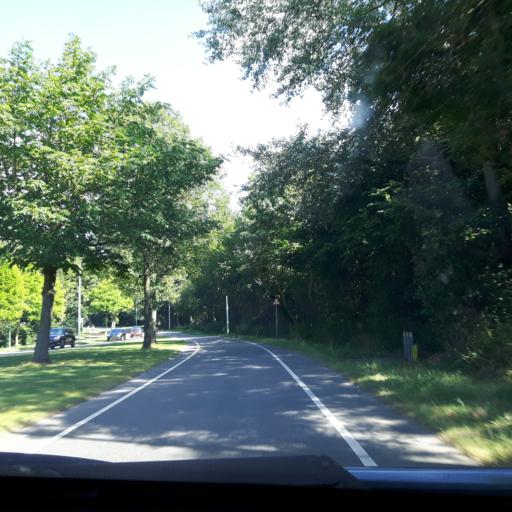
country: NL
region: Zeeland
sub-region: Gemeente Goes
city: Goes
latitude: 51.5090
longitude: 3.8943
